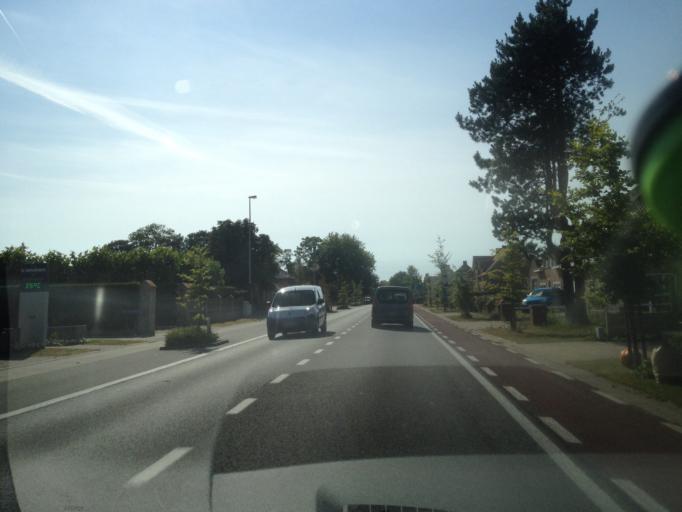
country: BE
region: Flanders
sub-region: Provincie West-Vlaanderen
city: Jabbeke
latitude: 51.1791
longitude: 3.1031
